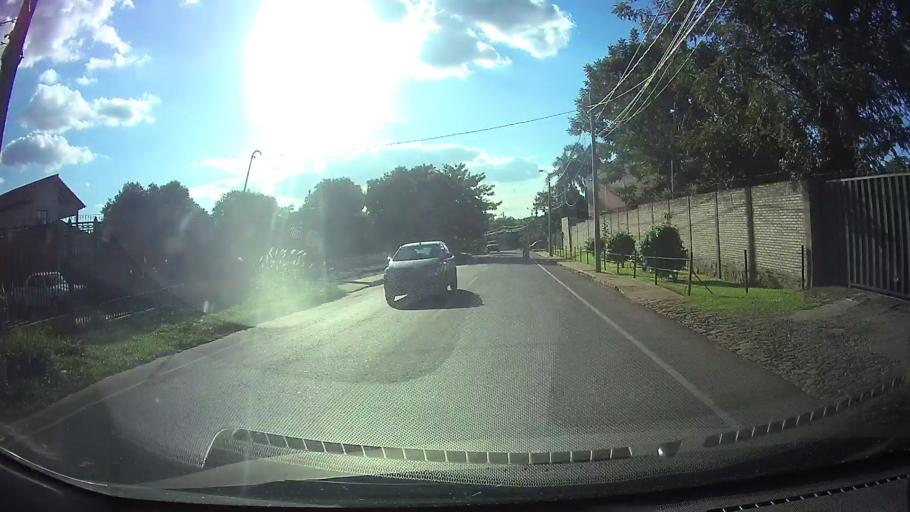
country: PY
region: Central
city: San Lorenzo
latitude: -25.2868
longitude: -57.5013
